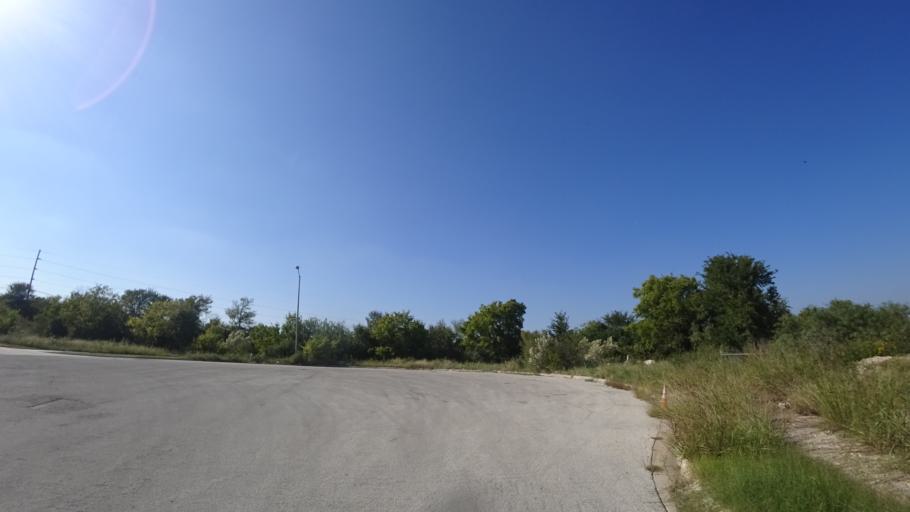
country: US
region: Texas
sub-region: Travis County
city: Austin
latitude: 30.3447
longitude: -97.6851
